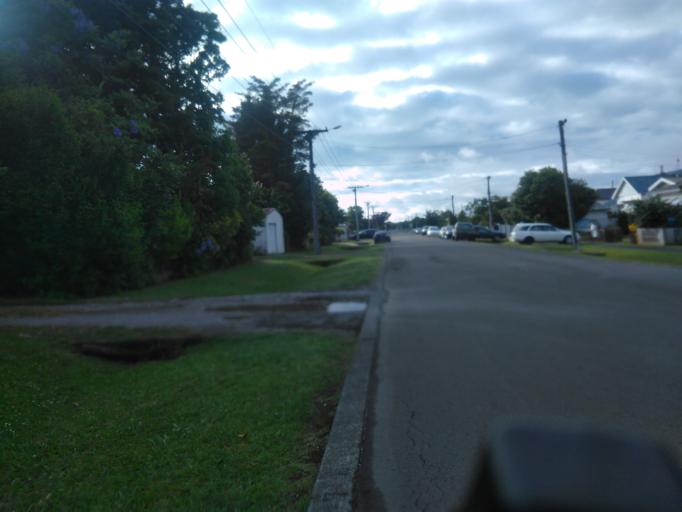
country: NZ
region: Gisborne
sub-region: Gisborne District
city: Gisborne
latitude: -38.6530
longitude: 178.0251
